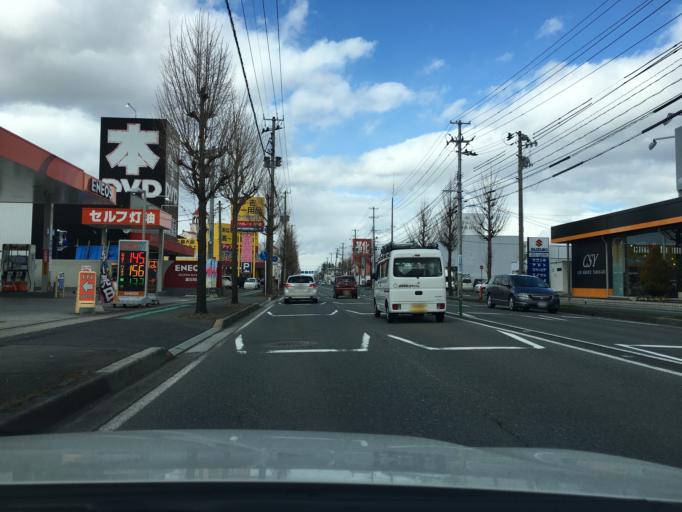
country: JP
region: Yamagata
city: Yamagata-shi
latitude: 38.2405
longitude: 140.3071
